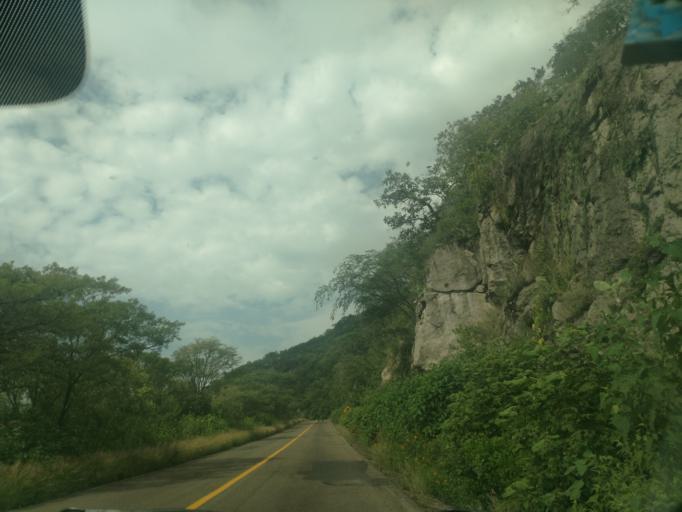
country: MX
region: Jalisco
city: El Salto
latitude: 20.3668
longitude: -104.5765
